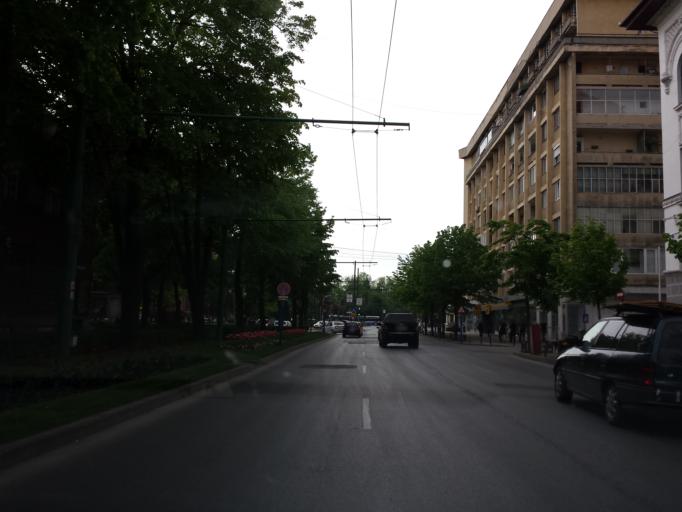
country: RO
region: Timis
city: Timisoara
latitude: 45.7509
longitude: 21.2263
